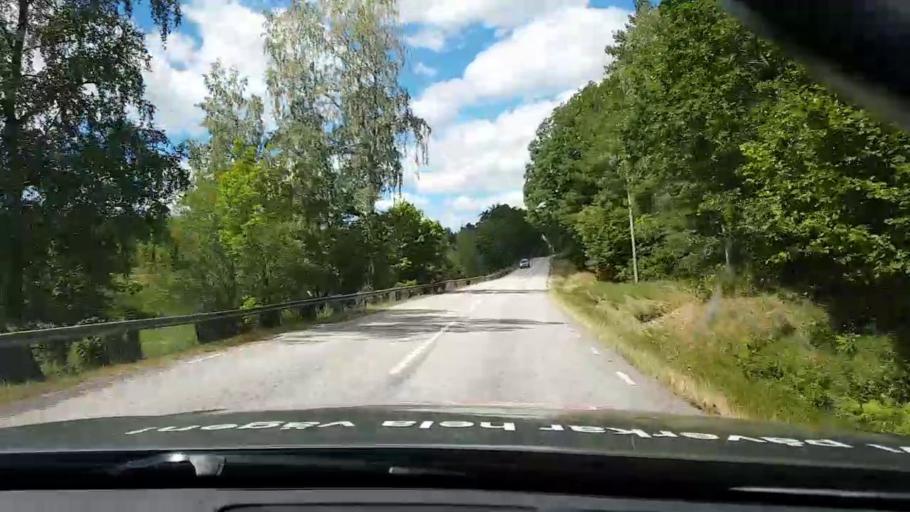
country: SE
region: Kalmar
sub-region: Vasterviks Kommun
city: Overum
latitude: 58.0747
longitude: 16.3644
